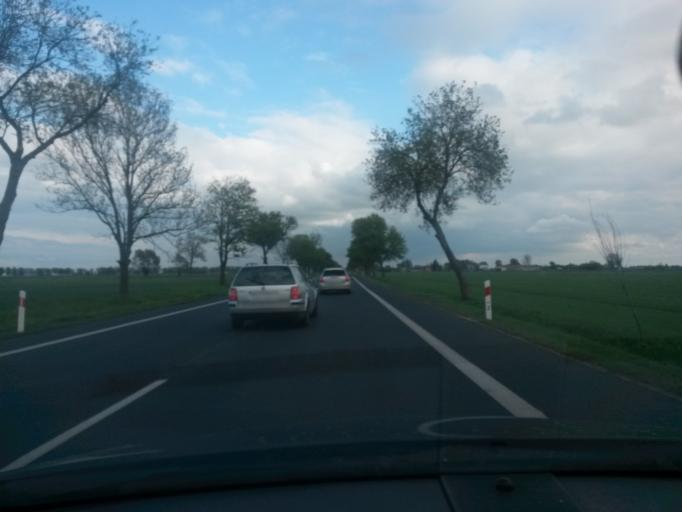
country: PL
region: Masovian Voivodeship
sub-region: Powiat plocki
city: Drobin
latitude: 52.7582
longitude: 19.9548
